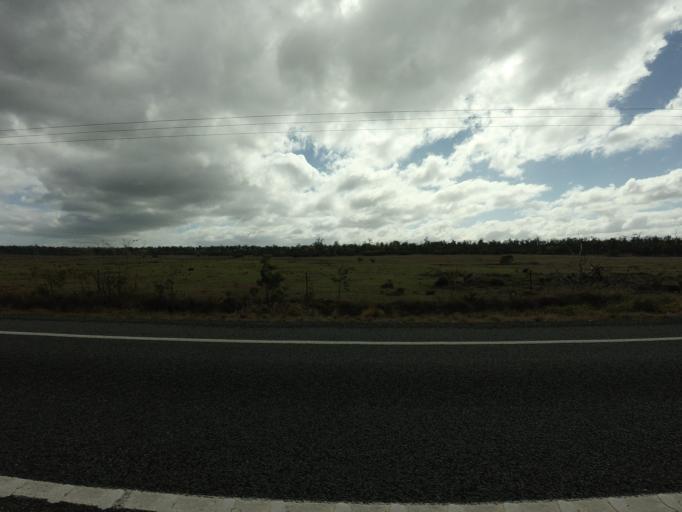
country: AU
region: Tasmania
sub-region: Northern Midlands
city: Evandale
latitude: -41.8311
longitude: 147.4843
